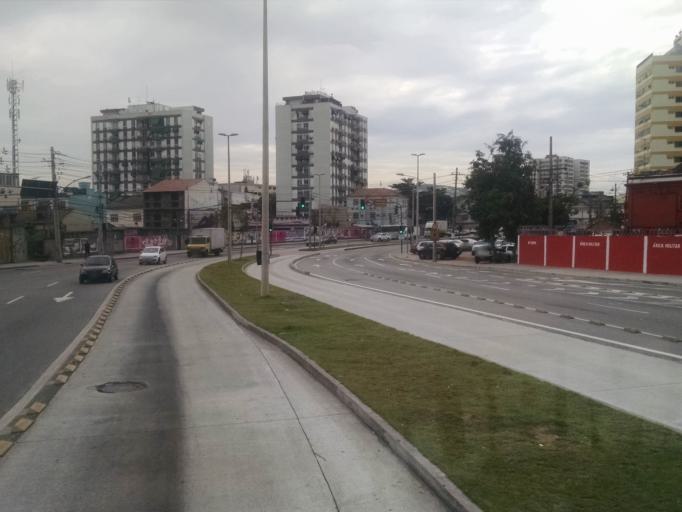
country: BR
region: Rio de Janeiro
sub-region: Sao Joao De Meriti
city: Sao Joao de Meriti
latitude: -22.8805
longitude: -43.3417
